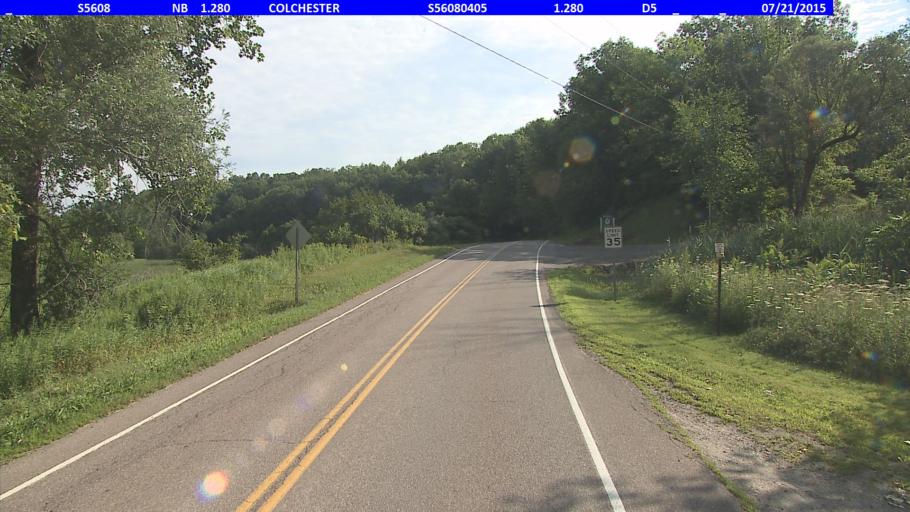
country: US
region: Vermont
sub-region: Chittenden County
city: Winooski
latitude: 44.5173
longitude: -73.2023
